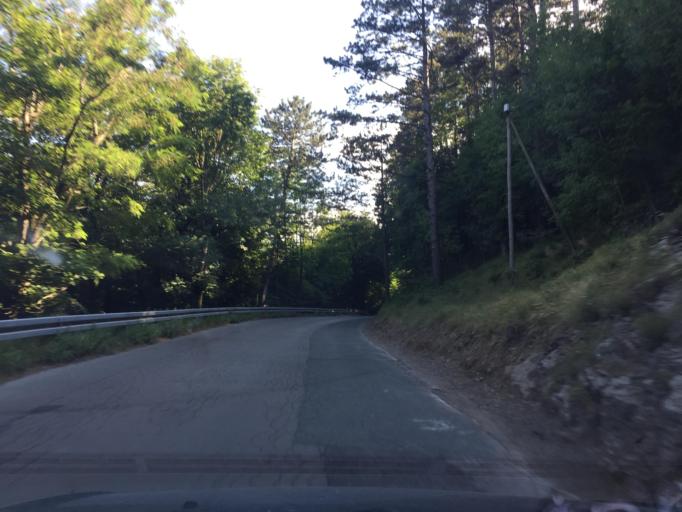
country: HR
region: Primorsko-Goranska
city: Klana
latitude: 45.4546
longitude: 14.3783
